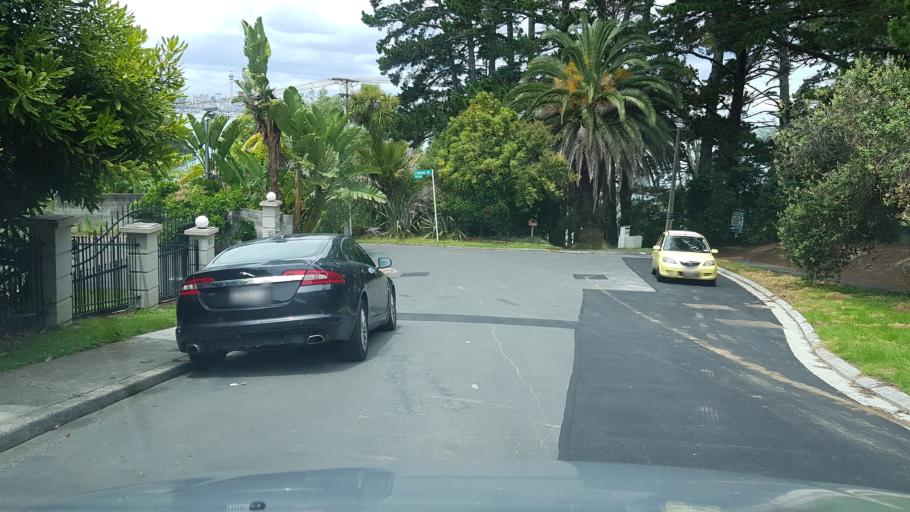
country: NZ
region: Auckland
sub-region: Auckland
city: North Shore
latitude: -36.8175
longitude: 174.7258
